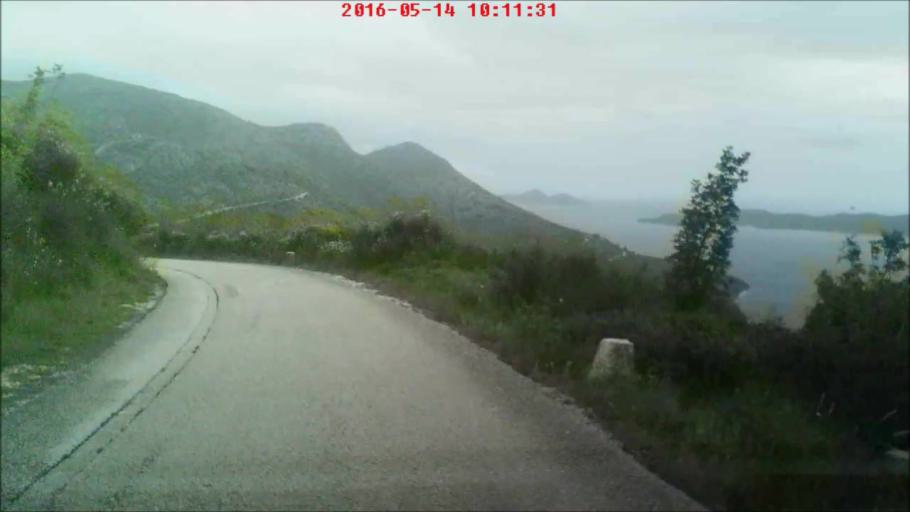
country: HR
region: Dubrovacko-Neretvanska
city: Podgora
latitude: 42.7356
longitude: 17.9442
